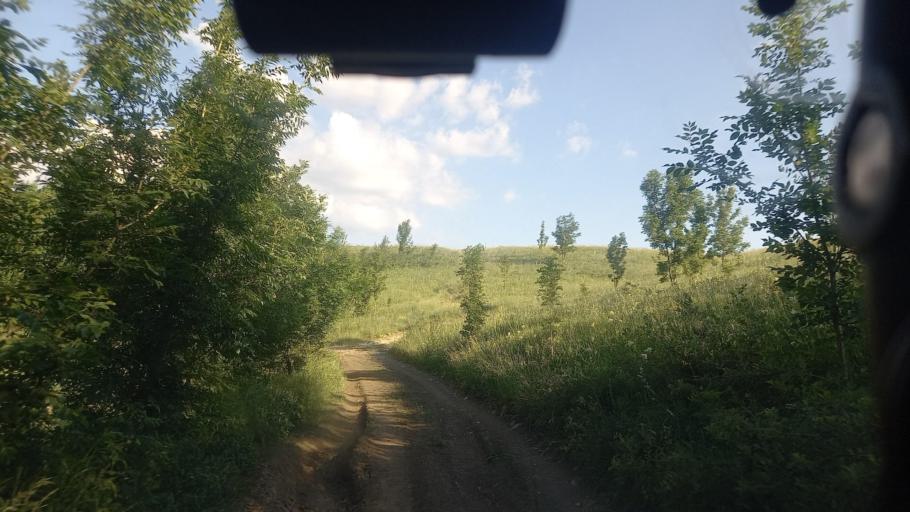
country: RU
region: Krasnodarskiy
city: Gelendzhik
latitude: 44.6190
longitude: 38.1888
